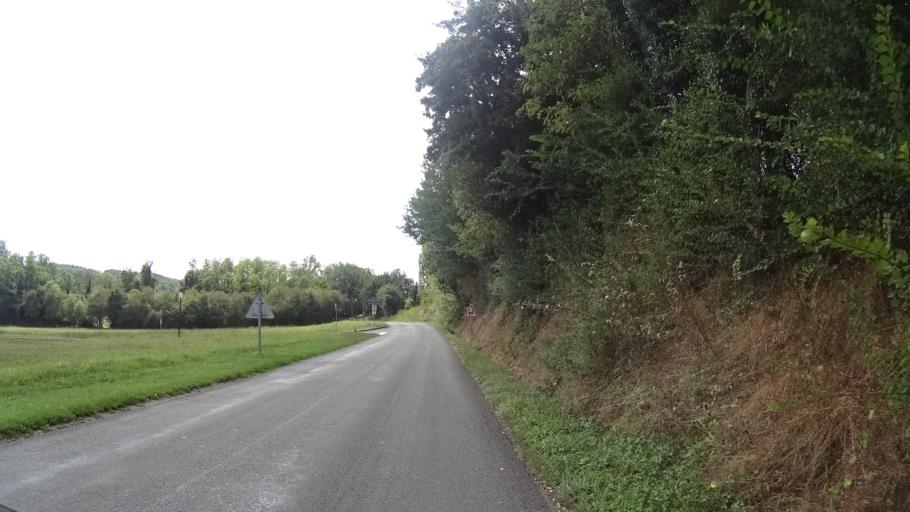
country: FR
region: Aquitaine
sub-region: Departement du Lot-et-Garonne
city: Pont-du-Casse
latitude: 44.2653
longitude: 0.7041
